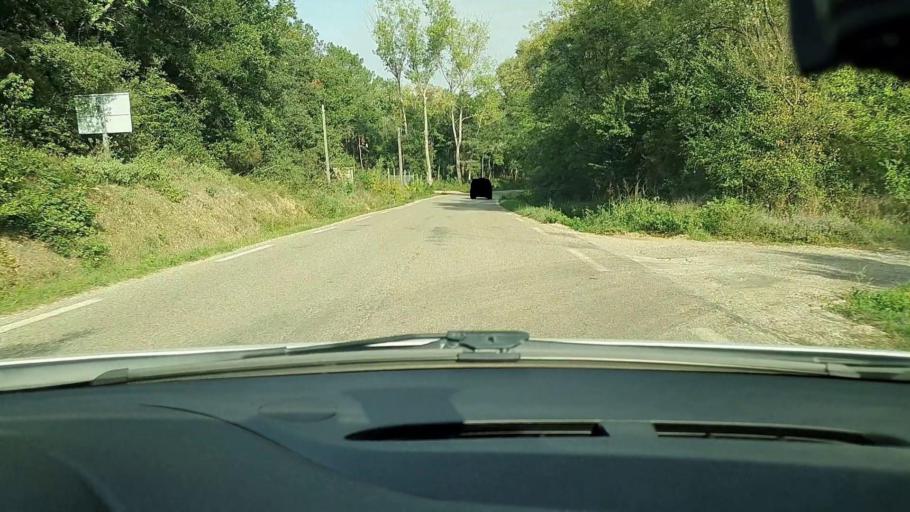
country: FR
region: Languedoc-Roussillon
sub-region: Departement du Gard
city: Saint-Quentin-la-Poterie
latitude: 44.0978
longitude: 4.4544
